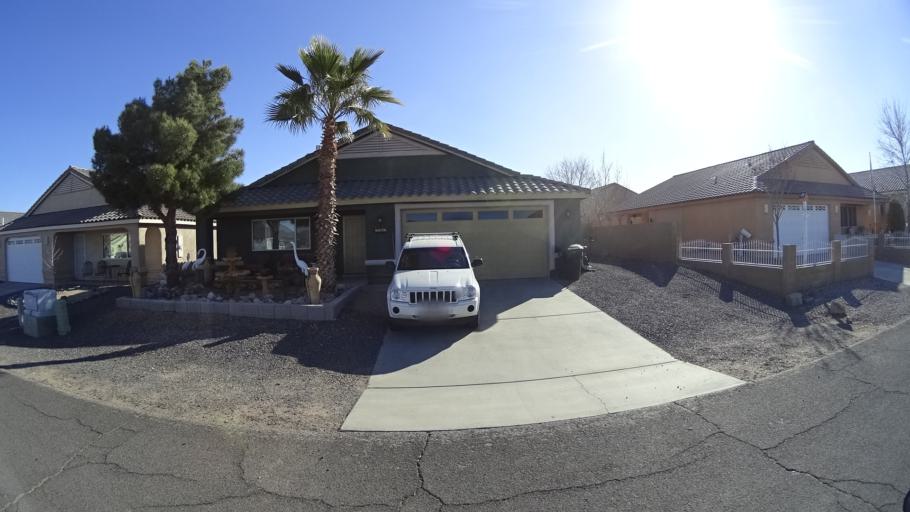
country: US
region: Arizona
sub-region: Mohave County
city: Kingman
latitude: 35.2128
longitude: -114.0068
